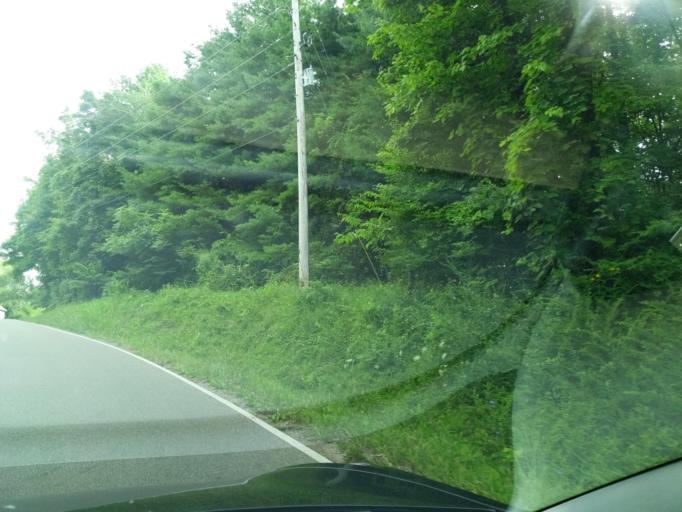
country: US
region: Ohio
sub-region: Fairfield County
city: Lancaster
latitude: 39.5677
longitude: -82.5922
